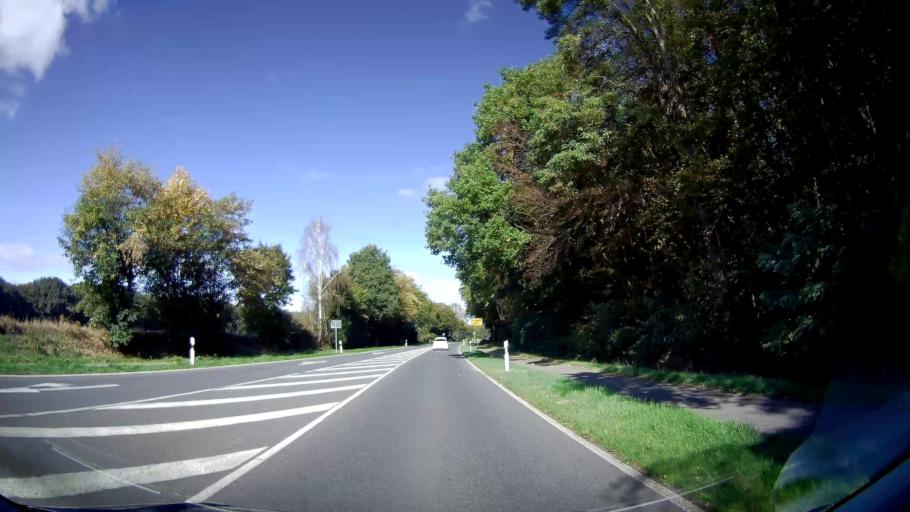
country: DE
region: North Rhine-Westphalia
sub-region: Regierungsbezirk Dusseldorf
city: Dinslaken
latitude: 51.6045
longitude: 6.7556
